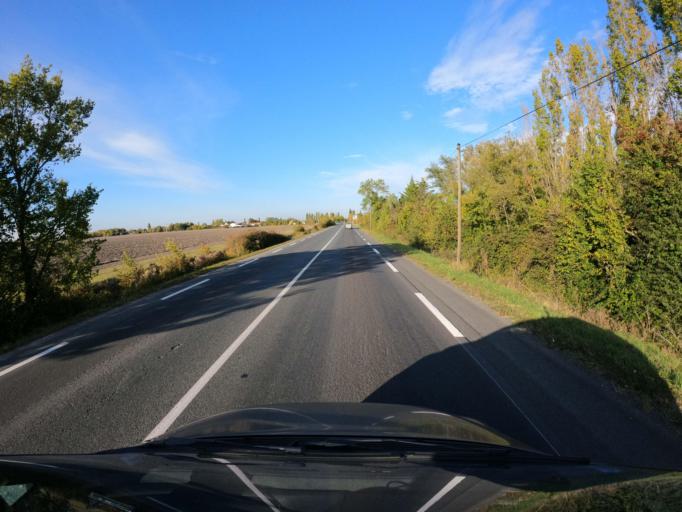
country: FR
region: Pays de la Loire
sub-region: Departement de la Vendee
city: Chaille-les-Marais
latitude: 46.3607
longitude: -0.9900
